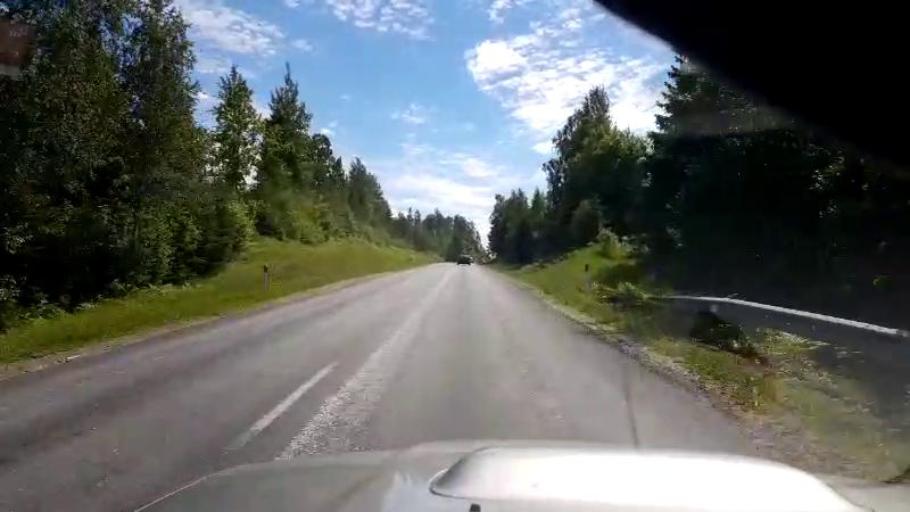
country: EE
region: Jogevamaa
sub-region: Jogeva linn
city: Jogeva
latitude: 58.8422
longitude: 26.2908
